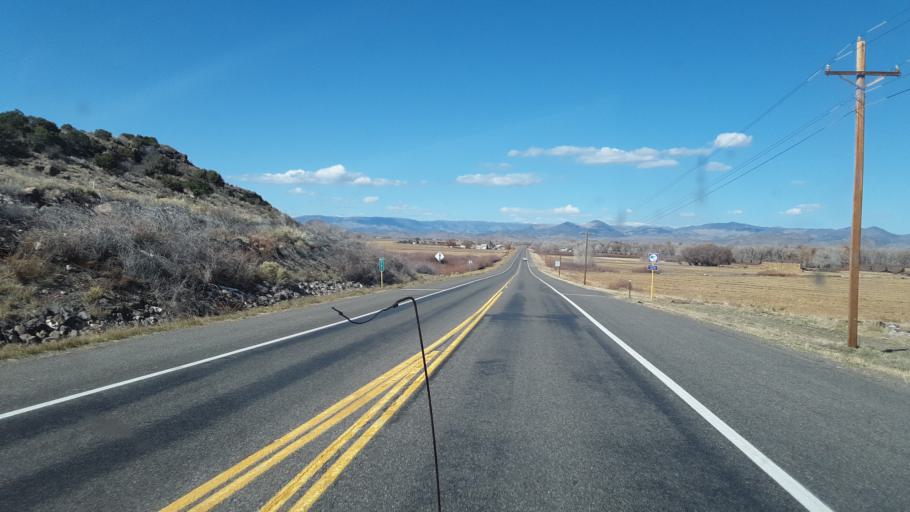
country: US
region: Colorado
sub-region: Rio Grande County
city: Del Norte
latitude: 37.6496
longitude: -106.2749
